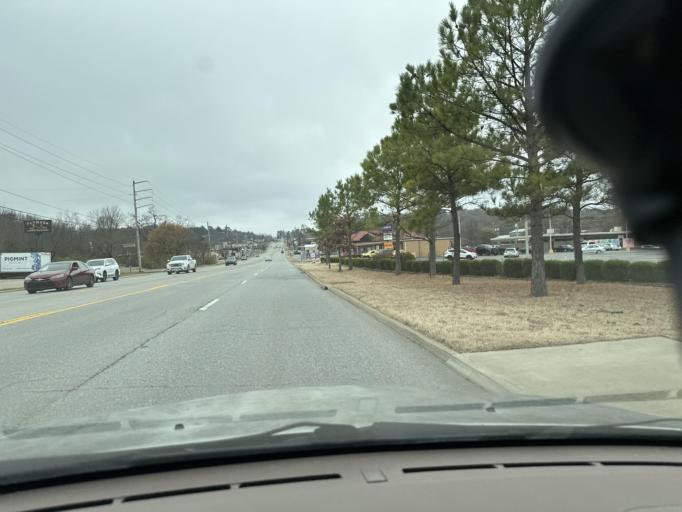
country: US
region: Arkansas
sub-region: Washington County
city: Fayetteville
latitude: 36.0896
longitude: -94.1543
